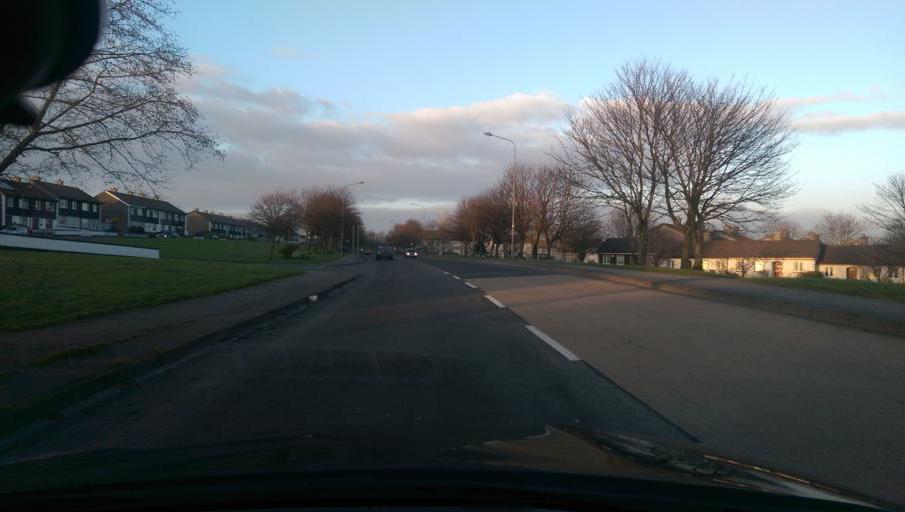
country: IE
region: Connaught
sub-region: County Galway
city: Gaillimh
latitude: 53.2780
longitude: -9.0786
